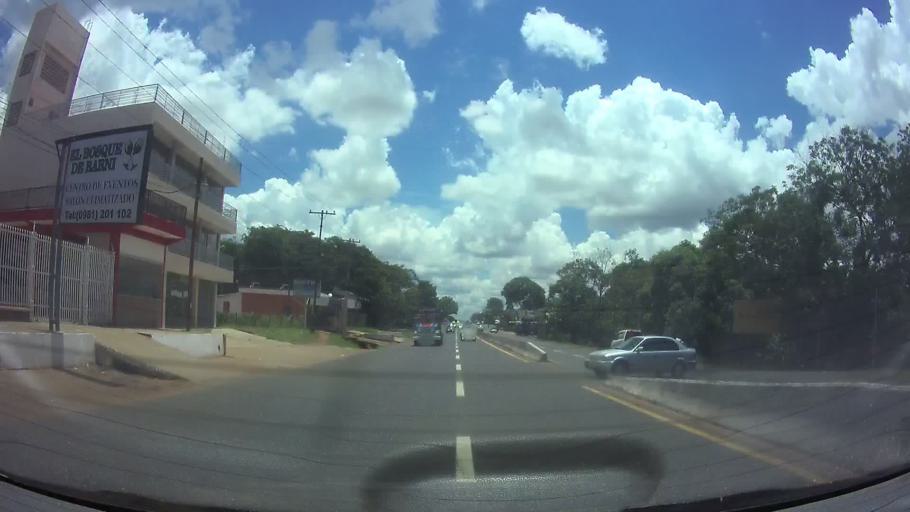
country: PY
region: Central
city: Itaugua
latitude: -25.3788
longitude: -57.3858
